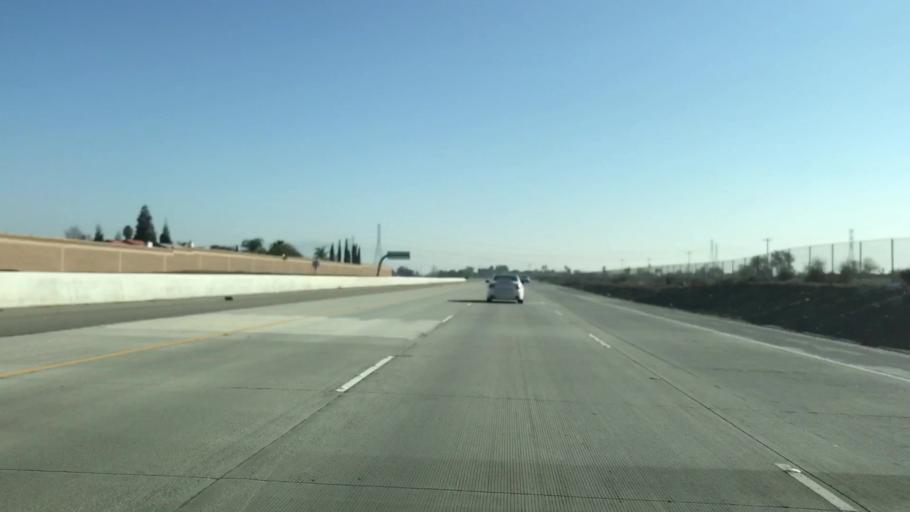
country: US
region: California
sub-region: Kern County
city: Greenacres
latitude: 35.3616
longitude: -119.1044
